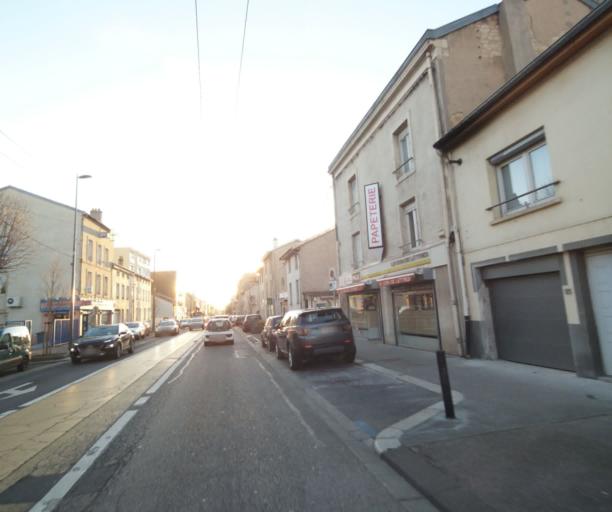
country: FR
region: Lorraine
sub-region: Departement de Meurthe-et-Moselle
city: Saint-Max
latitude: 48.7018
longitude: 6.2119
